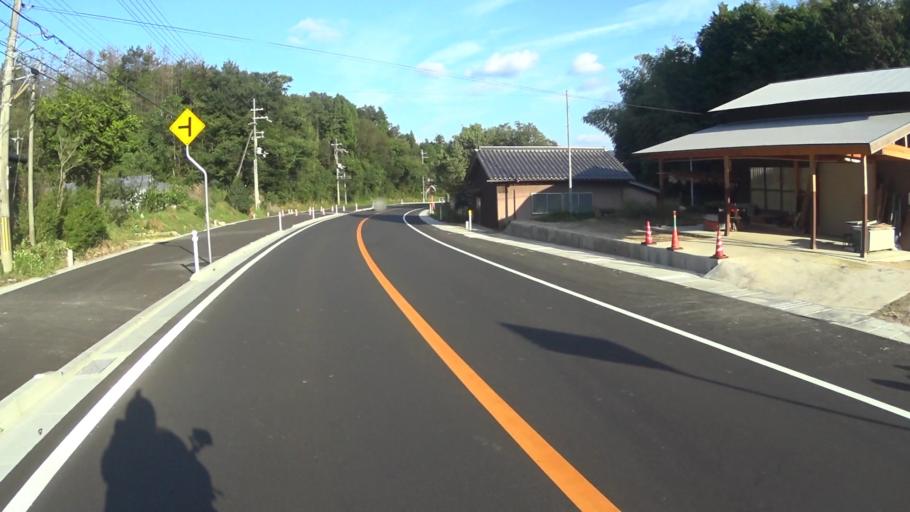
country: JP
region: Hyogo
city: Toyooka
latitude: 35.5910
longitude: 134.9383
